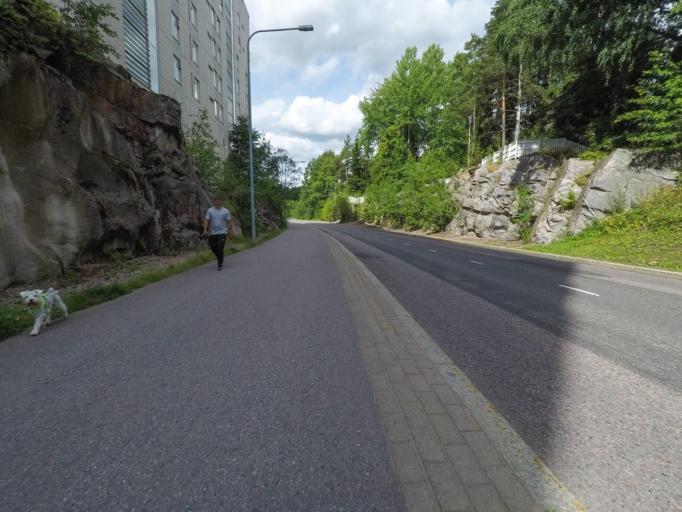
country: FI
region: Uusimaa
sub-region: Helsinki
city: Vantaa
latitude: 60.2305
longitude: 24.9968
